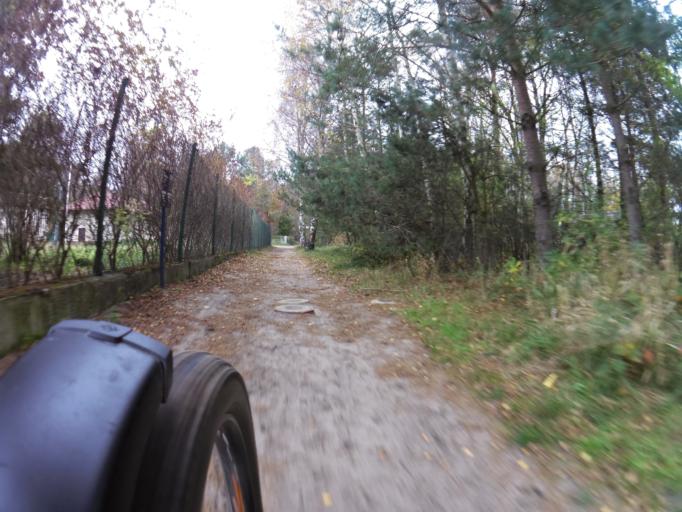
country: PL
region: Pomeranian Voivodeship
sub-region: Powiat pucki
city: Wierzchucino
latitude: 54.8273
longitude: 18.0814
